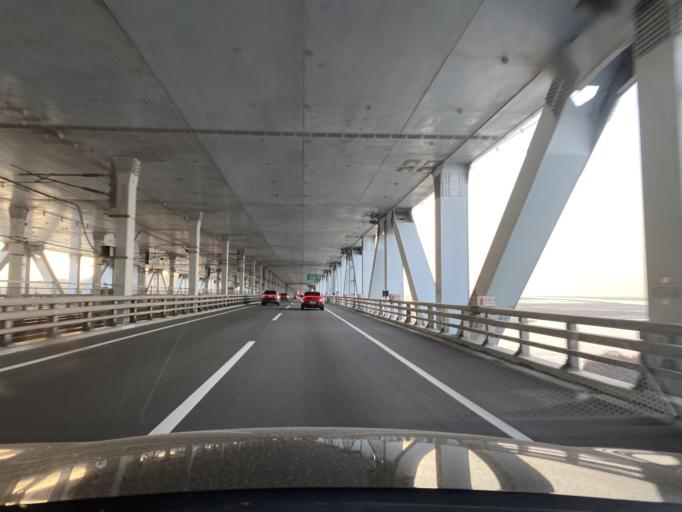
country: KR
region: Gyeonggi-do
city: Tongjin
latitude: 37.5451
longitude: 126.5825
